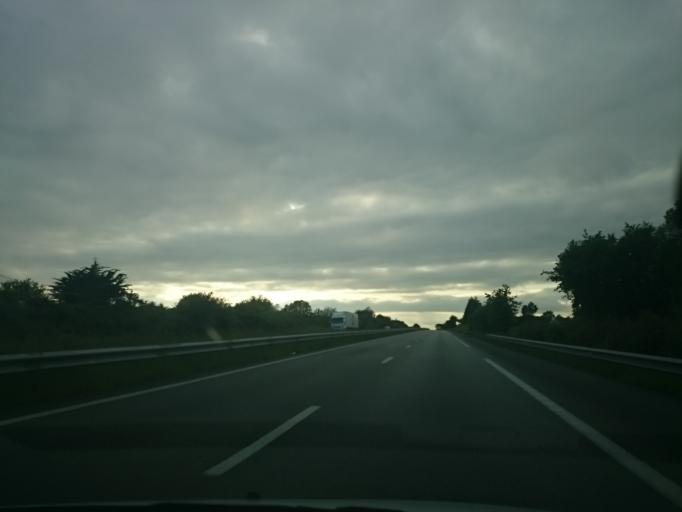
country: FR
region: Brittany
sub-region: Departement du Morbihan
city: Landaul
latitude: 47.7204
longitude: -3.0676
